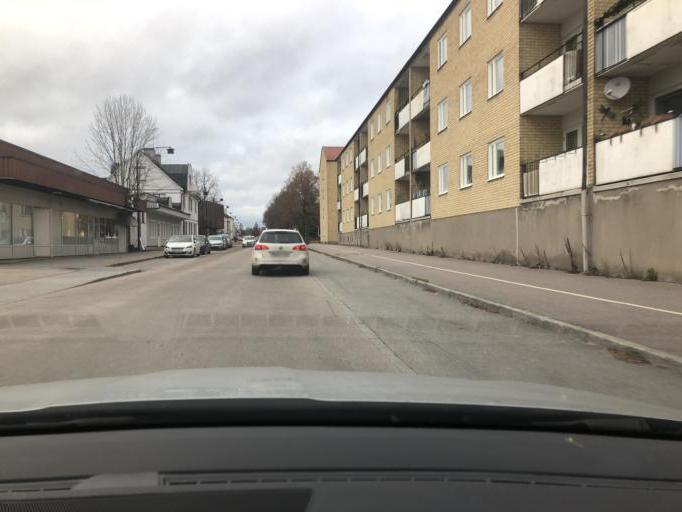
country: SE
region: Uppsala
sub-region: Tierps Kommun
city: Tierp
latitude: 60.3417
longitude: 17.5190
